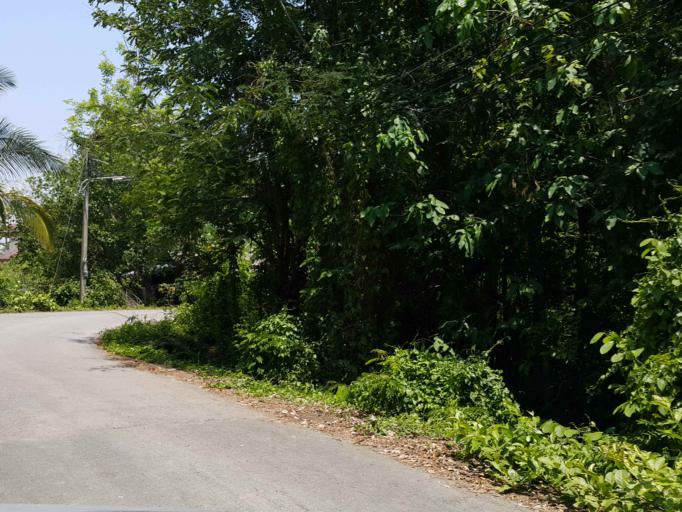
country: TH
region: Chiang Mai
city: San Sai
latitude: 18.8341
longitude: 99.1075
